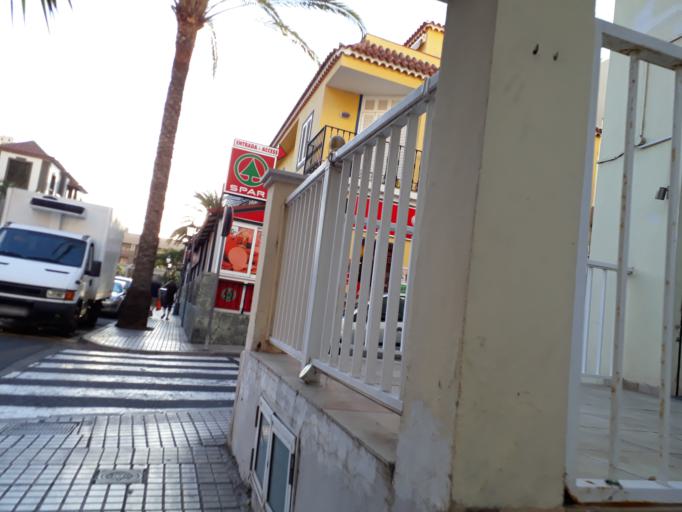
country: ES
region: Canary Islands
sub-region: Provincia de Santa Cruz de Tenerife
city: Alajero
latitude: 28.0958
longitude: -17.3427
